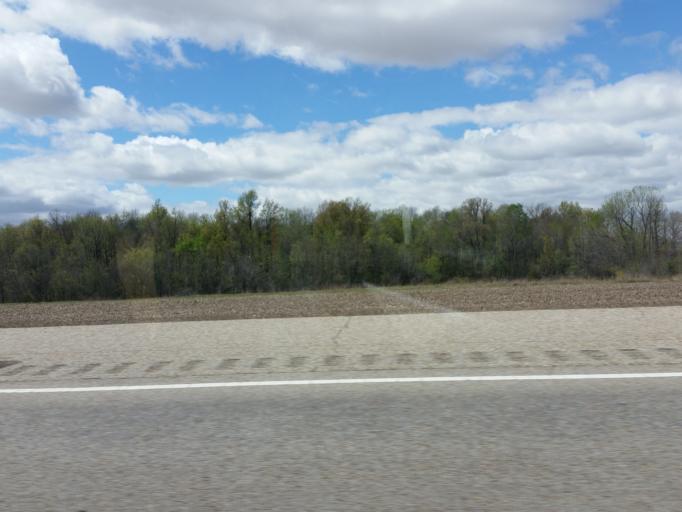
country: US
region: Arkansas
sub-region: Craighead County
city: Bay
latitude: 35.7191
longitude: -90.5800
